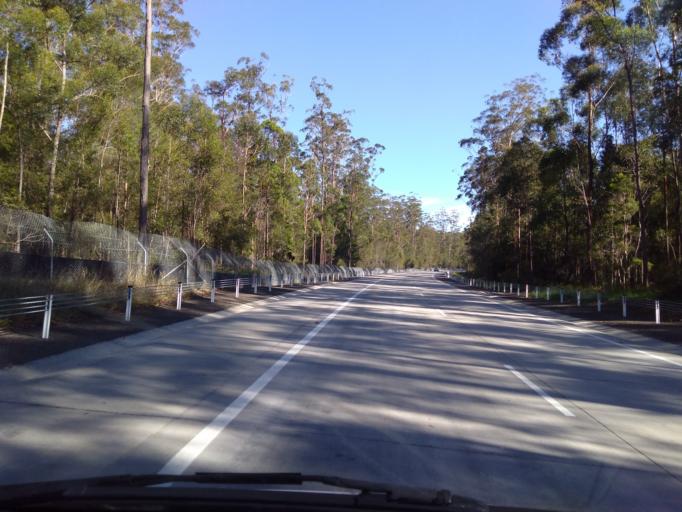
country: AU
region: New South Wales
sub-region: Port Macquarie-Hastings
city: North Shore
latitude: -31.3720
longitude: 152.8013
